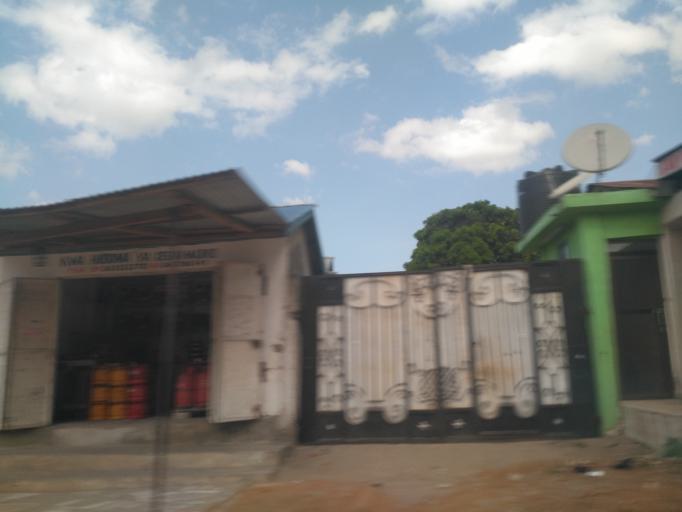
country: TZ
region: Dar es Salaam
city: Dar es Salaam
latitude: -6.8959
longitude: 39.2837
